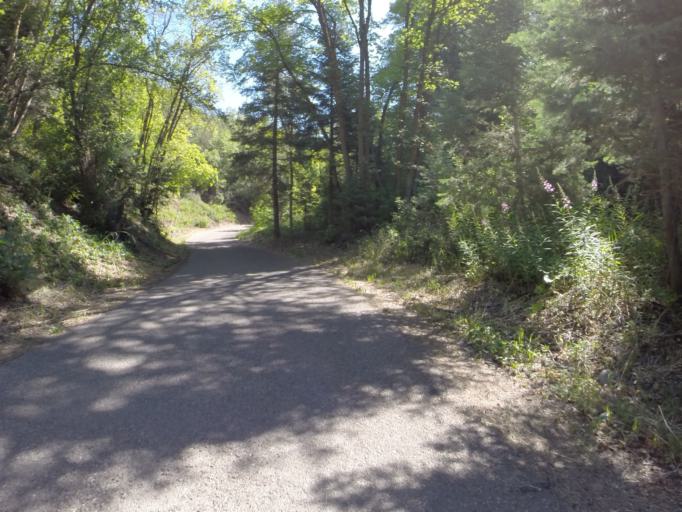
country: US
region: Utah
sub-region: Davis County
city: Woods Cross
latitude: 40.8182
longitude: -111.8200
